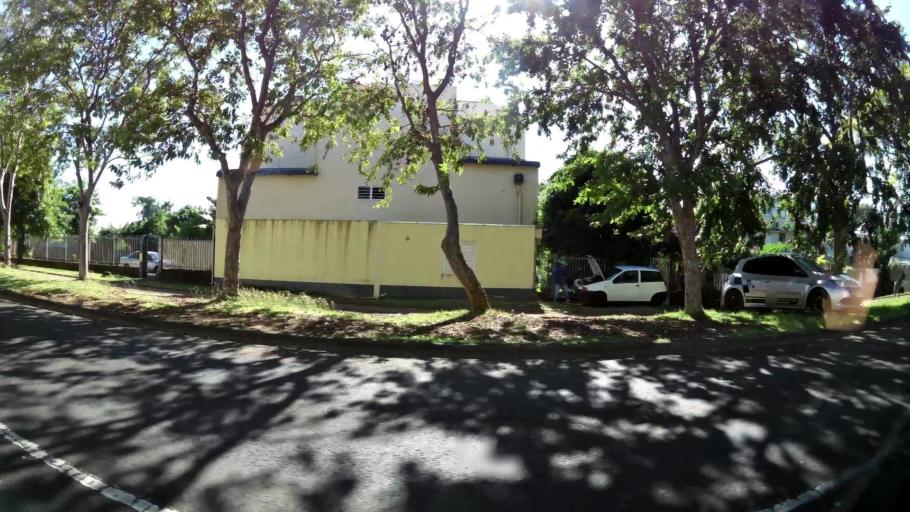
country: RE
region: Reunion
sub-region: Reunion
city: Saint-Denis
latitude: -20.8978
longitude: 55.4841
